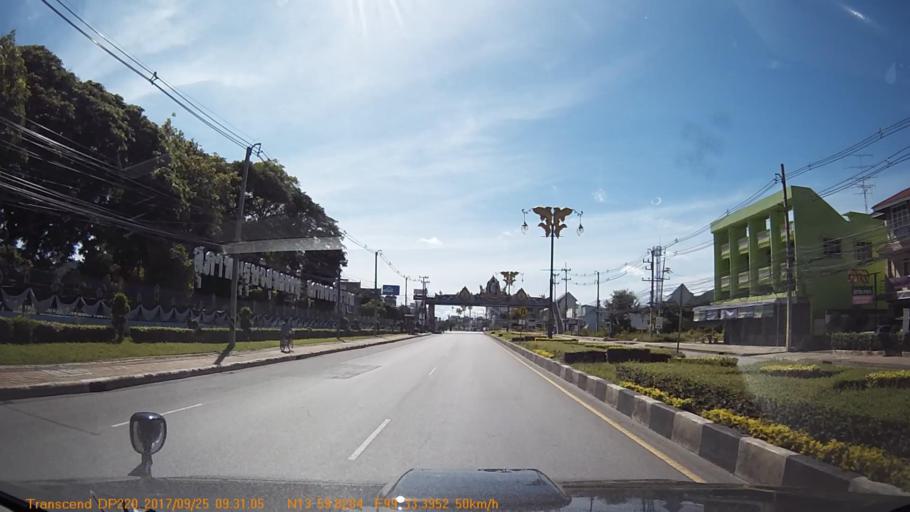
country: TH
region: Kanchanaburi
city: Kanchanaburi
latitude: 13.9970
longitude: 99.5568
